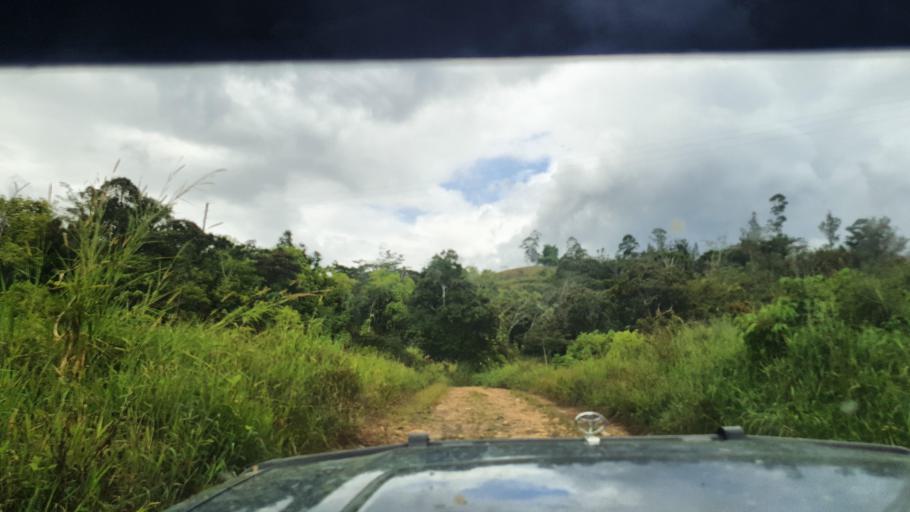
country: PG
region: Jiwaka
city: Minj
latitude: -5.8925
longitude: 144.8163
